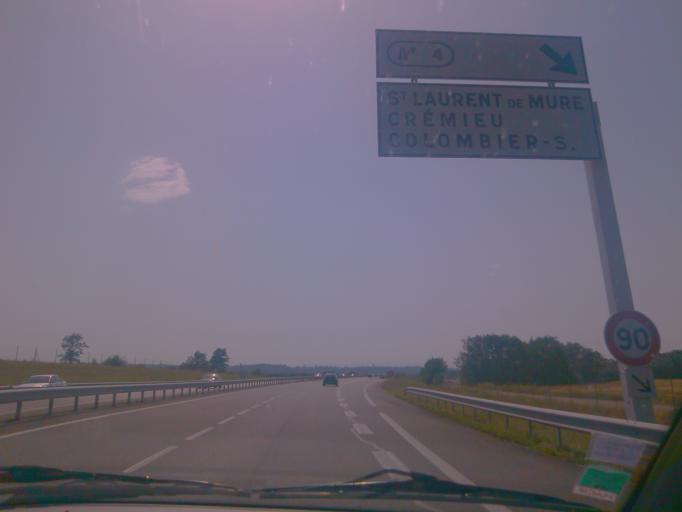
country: FR
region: Rhone-Alpes
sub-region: Departement du Rhone
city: Pusignan
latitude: 45.7683
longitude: 5.0841
